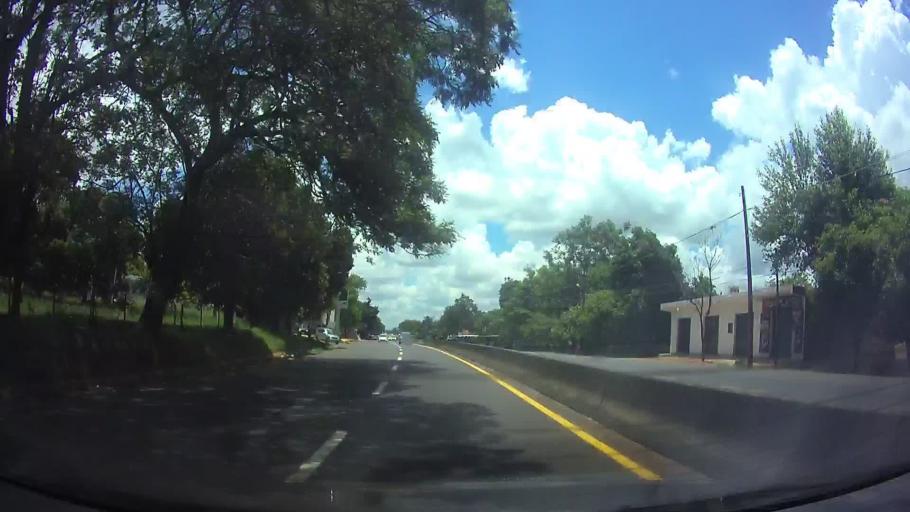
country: PY
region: Central
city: Itaugua
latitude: -25.3791
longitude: -57.3818
